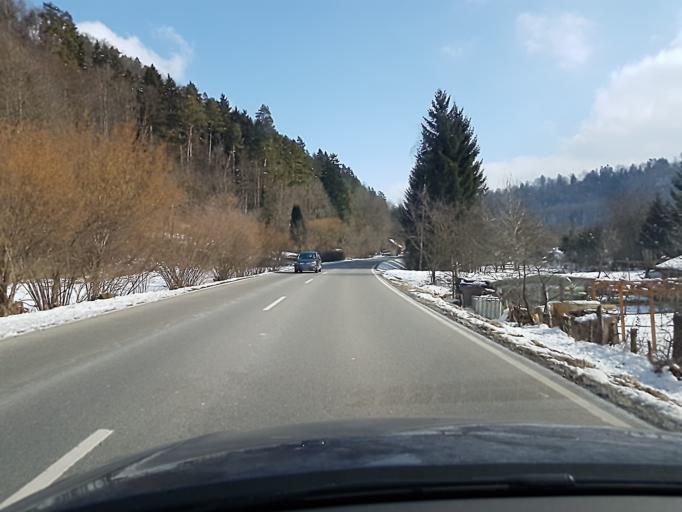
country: DE
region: Baden-Wuerttemberg
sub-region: Freiburg Region
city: Sulz am Neckar
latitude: 48.3592
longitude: 8.6143
